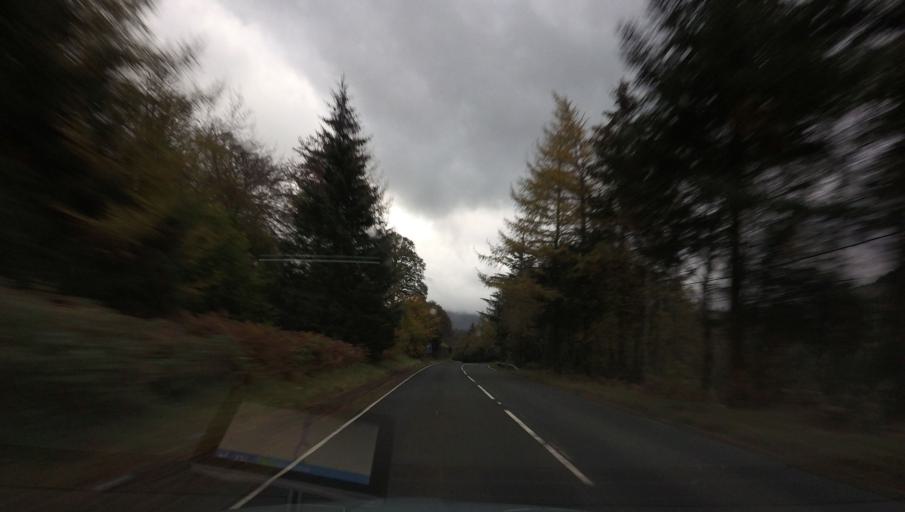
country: GB
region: Scotland
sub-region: Stirling
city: Callander
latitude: 56.3396
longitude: -4.3256
